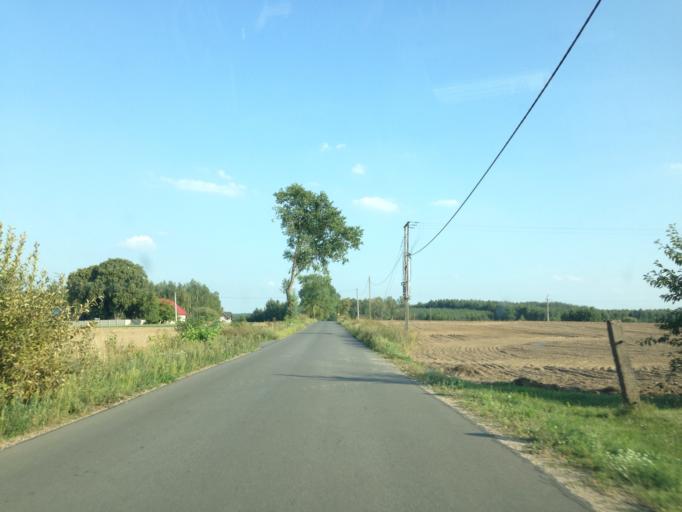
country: PL
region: Warmian-Masurian Voivodeship
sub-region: Powiat nowomiejski
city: Biskupiec
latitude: 53.4219
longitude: 19.3155
